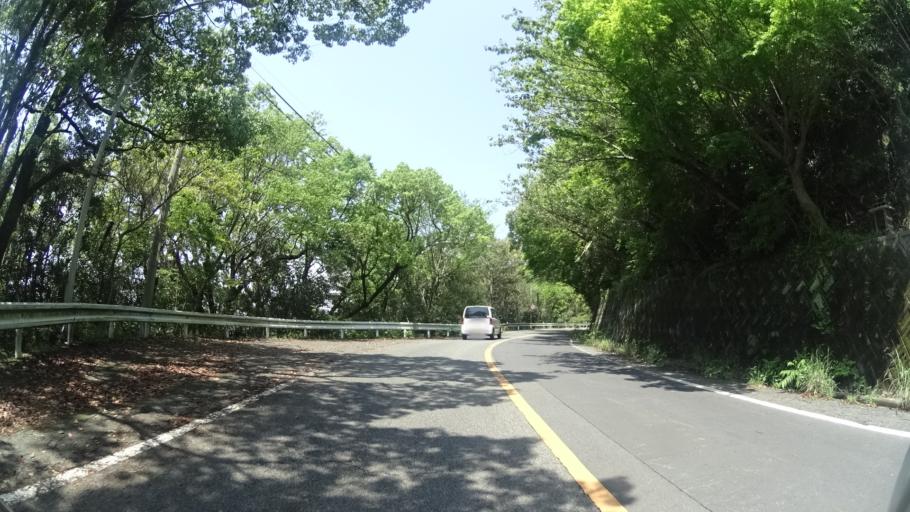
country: JP
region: Tokushima
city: Tokushima-shi
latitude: 34.0653
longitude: 134.5337
